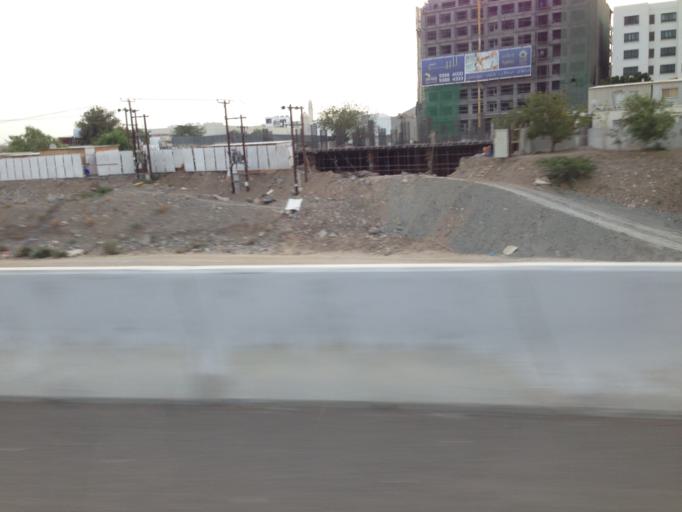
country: OM
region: Muhafazat Masqat
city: Bawshar
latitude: 23.5857
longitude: 58.4438
